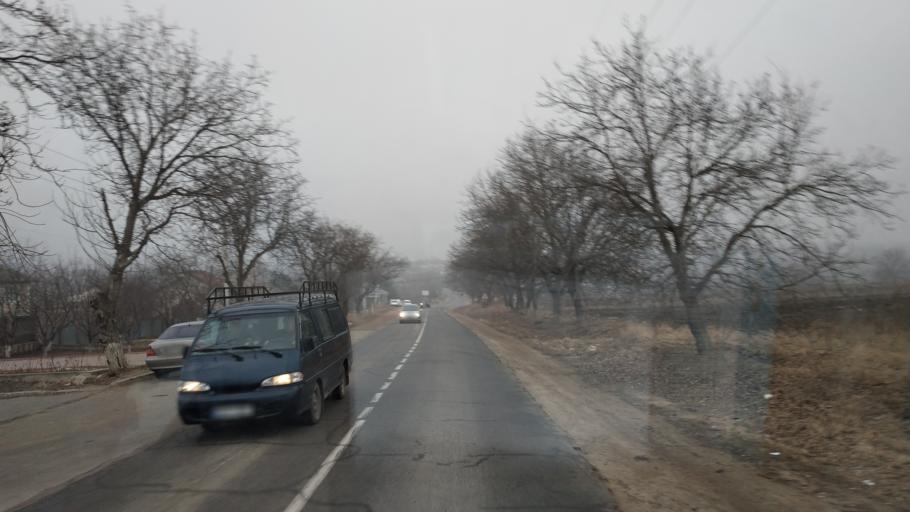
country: MD
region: Laloveni
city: Ialoveni
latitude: 46.9382
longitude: 28.7964
